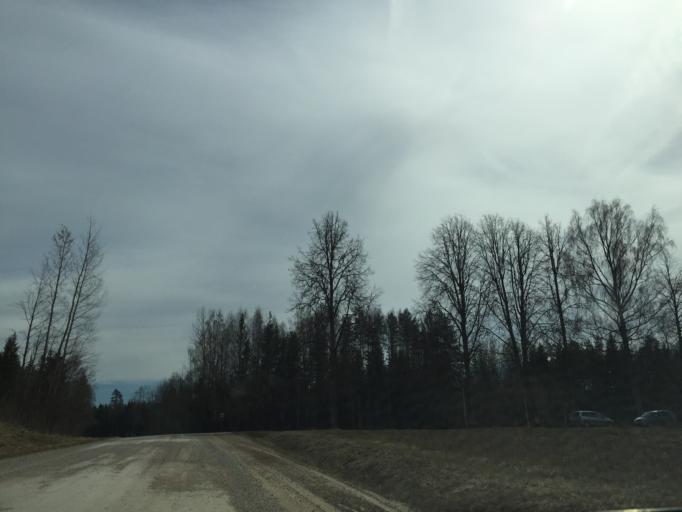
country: LV
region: Valkas Rajons
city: Valka
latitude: 57.8033
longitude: 25.9486
